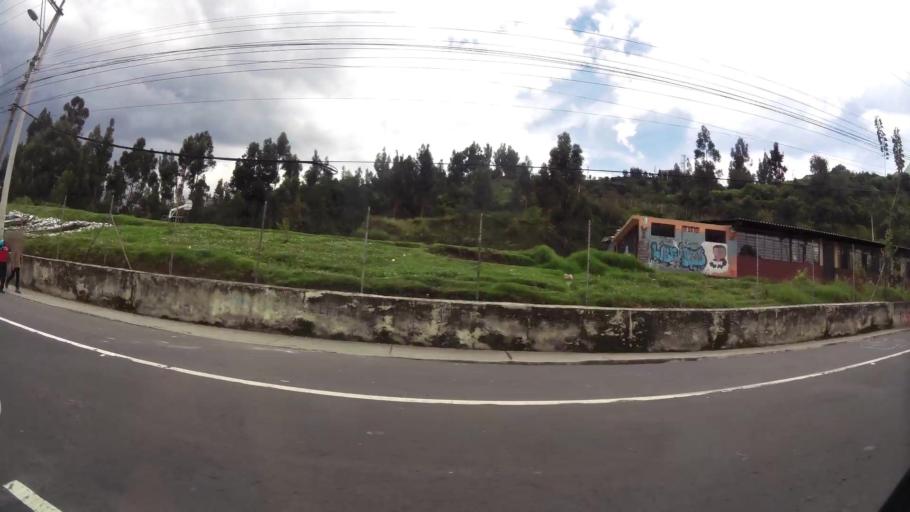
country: EC
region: Pichincha
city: Quito
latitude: -0.2923
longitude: -78.5352
